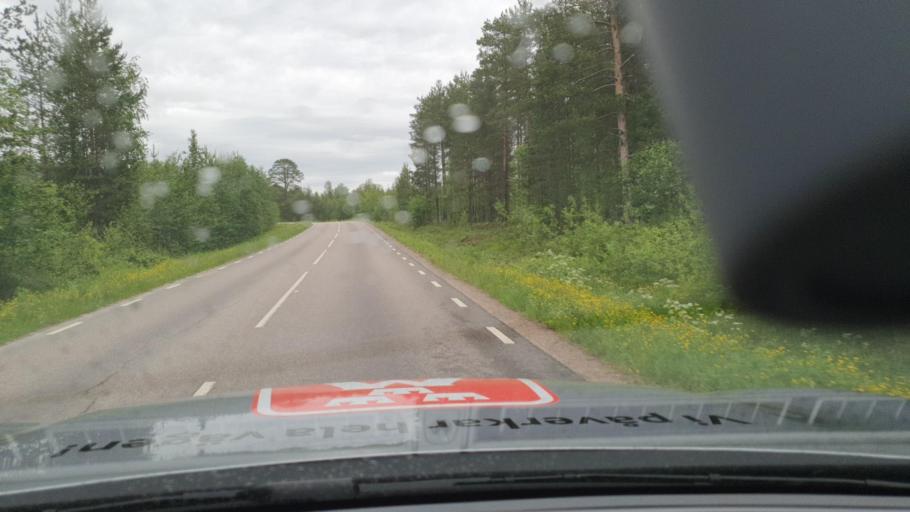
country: SE
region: Norrbotten
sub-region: Overkalix Kommun
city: OEverkalix
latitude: 66.3546
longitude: 22.8005
